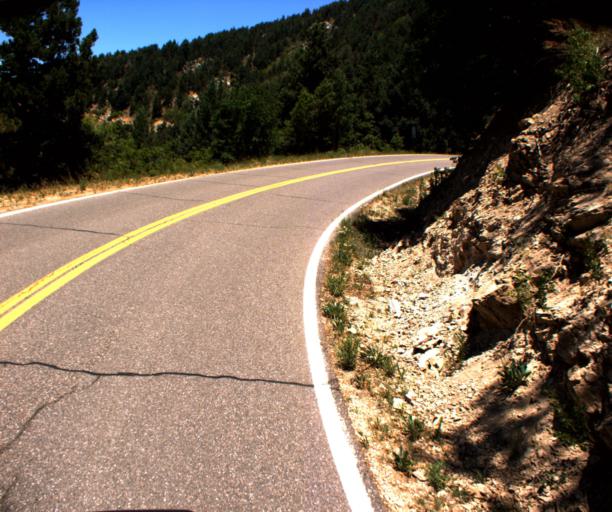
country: US
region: Arizona
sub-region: Graham County
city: Swift Trail Junction
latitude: 32.6444
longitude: -109.8565
